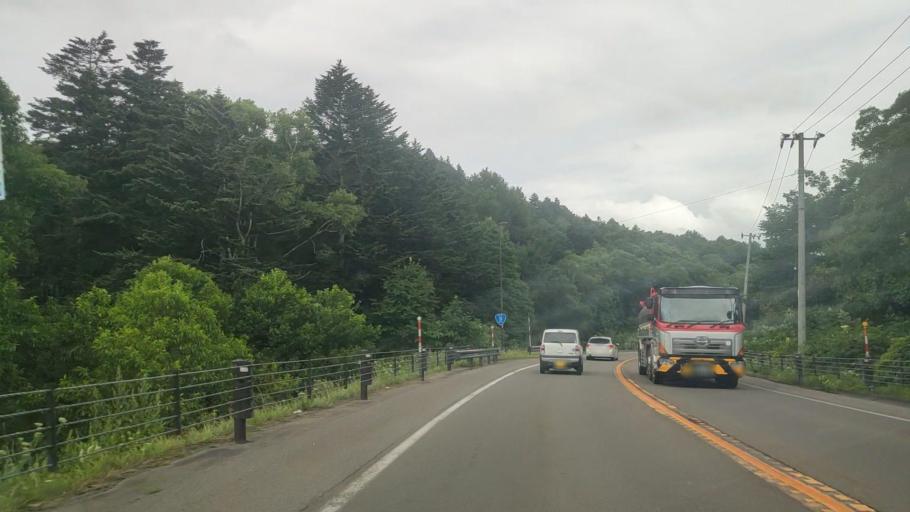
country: JP
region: Hokkaido
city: Nanae
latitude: 41.9673
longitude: 140.6500
